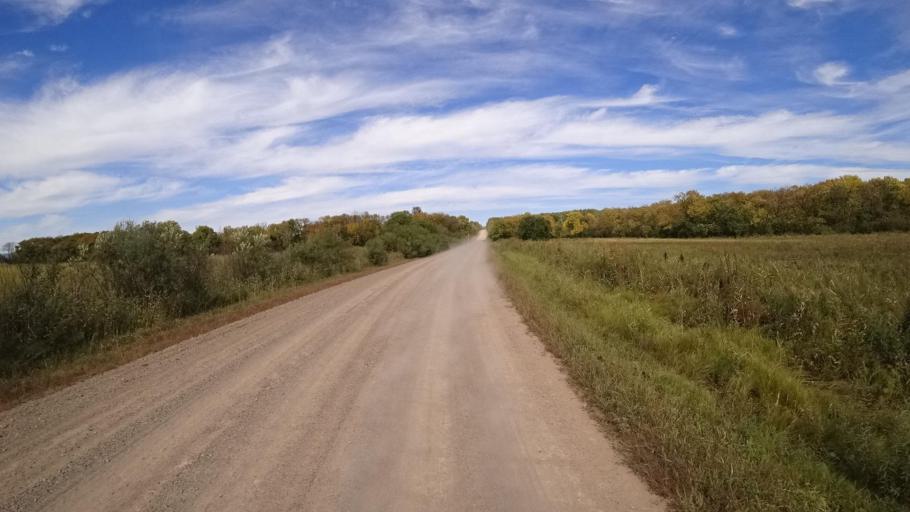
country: RU
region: Primorskiy
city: Yakovlevka
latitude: 44.6186
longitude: 133.5970
